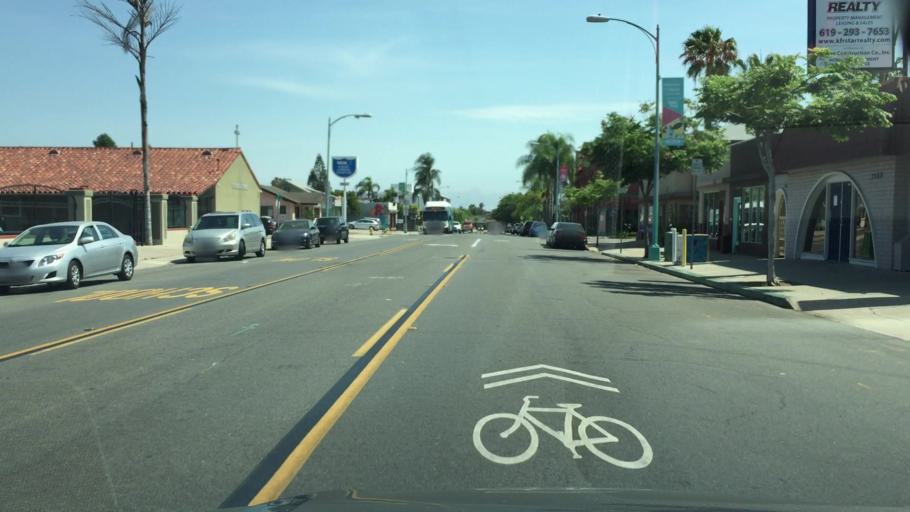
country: US
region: California
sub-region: San Diego County
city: San Diego
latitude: 32.7438
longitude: -117.1301
